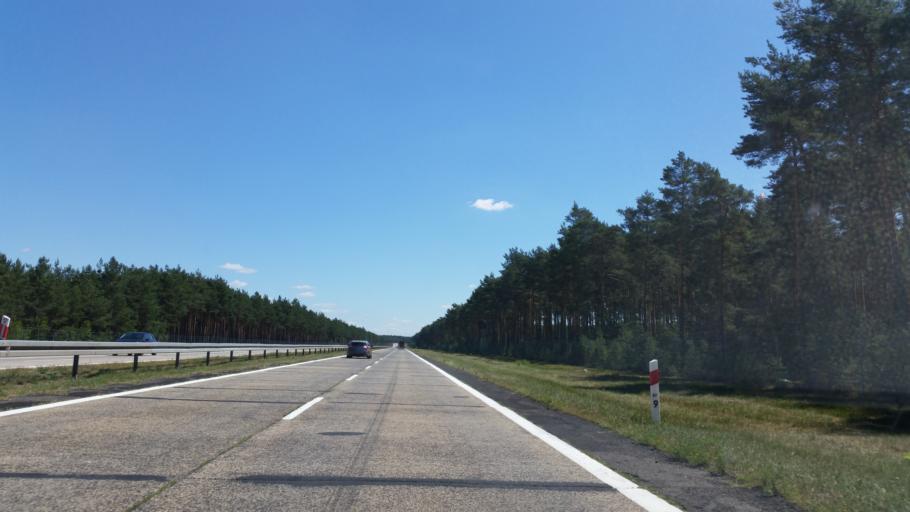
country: PL
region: Lubusz
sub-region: Powiat zaganski
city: Malomice
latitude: 51.4244
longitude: 15.4457
